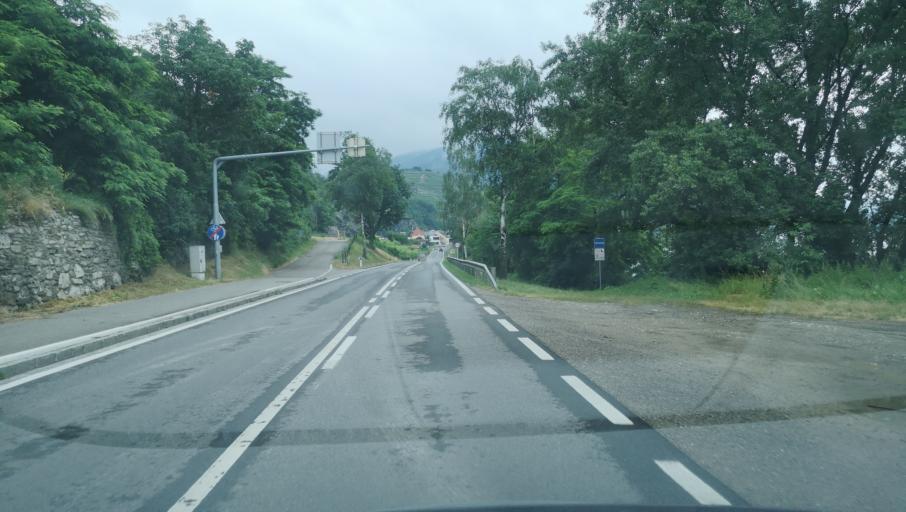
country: AT
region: Lower Austria
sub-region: Politischer Bezirk Krems
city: Spitz
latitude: 48.3534
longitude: 15.4068
